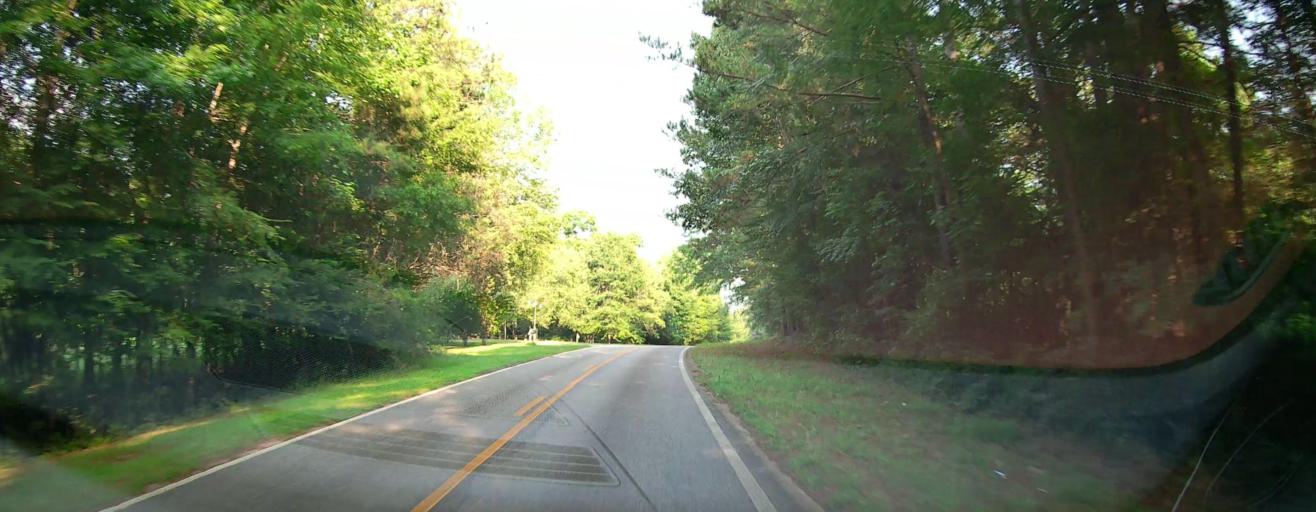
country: US
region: Georgia
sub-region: Monroe County
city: Forsyth
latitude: 33.0984
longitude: -83.7647
